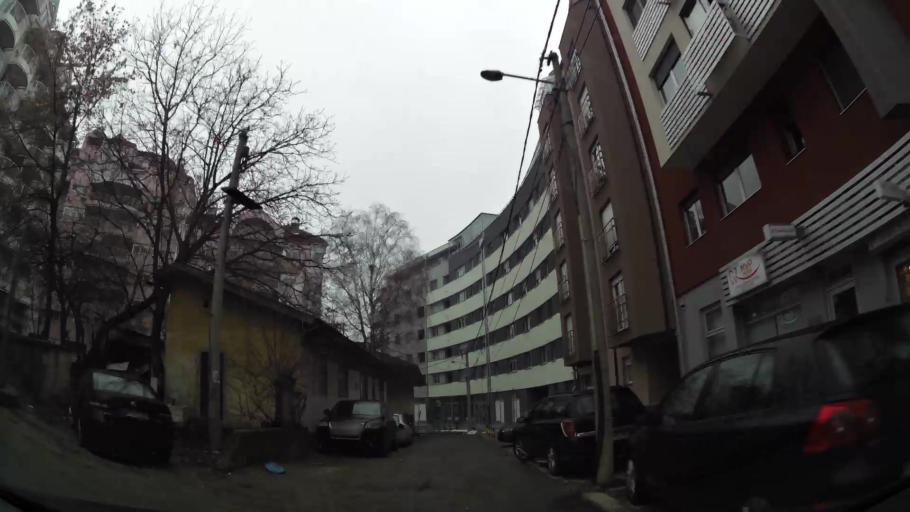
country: RS
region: Central Serbia
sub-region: Belgrade
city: Cukarica
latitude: 44.7845
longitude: 20.4224
